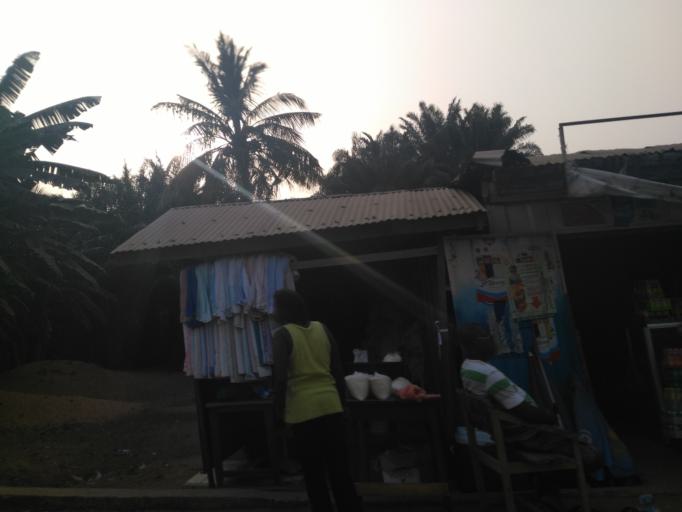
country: GH
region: Ashanti
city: Kumasi
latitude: 6.6858
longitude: -1.5987
